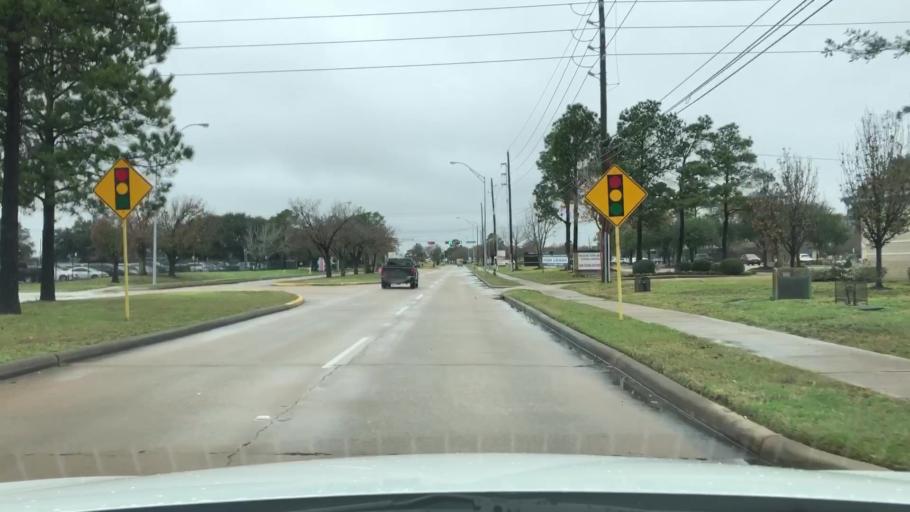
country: US
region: Texas
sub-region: Fort Bend County
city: Cinco Ranch
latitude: 29.7750
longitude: -95.7432
